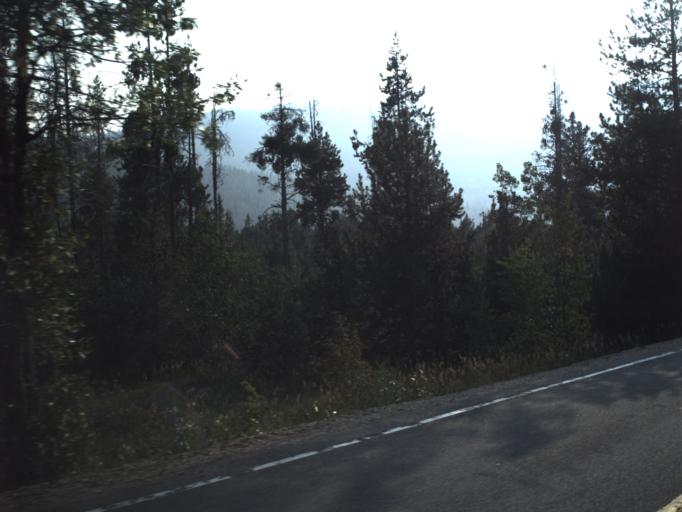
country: US
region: Utah
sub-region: Summit County
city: Francis
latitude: 40.5780
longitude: -111.0325
